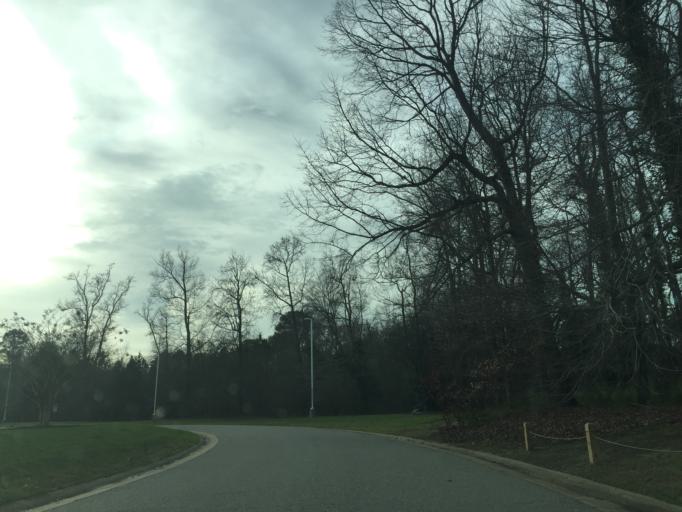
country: US
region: Virginia
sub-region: City of Newport News
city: Newport News
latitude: 37.0557
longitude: -76.4893
